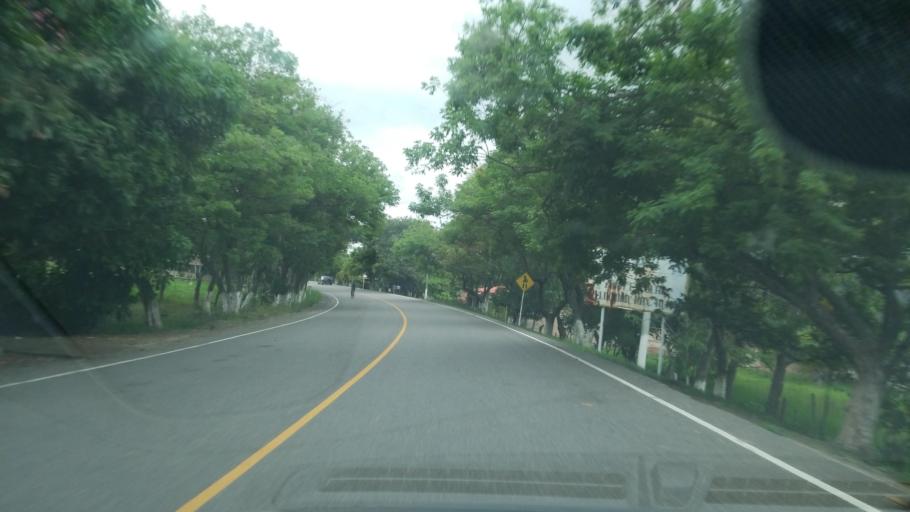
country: HN
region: Ocotepeque
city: Sinuapa
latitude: 14.5084
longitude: -89.2277
